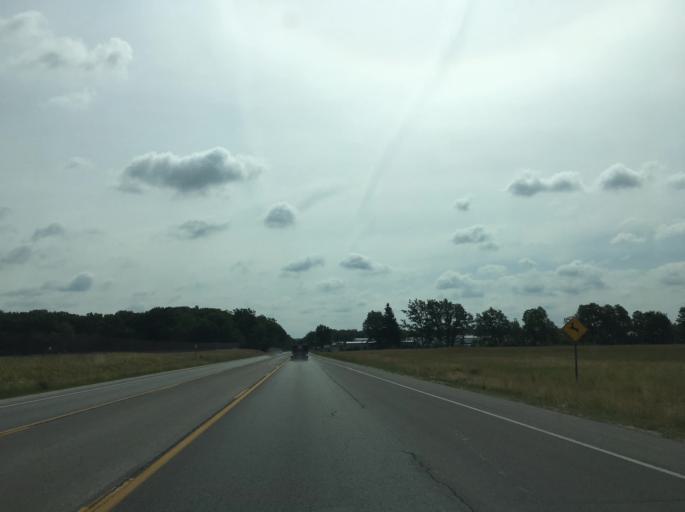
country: US
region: Michigan
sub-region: Grand Traverse County
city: Traverse City
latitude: 44.7333
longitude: -85.5888
